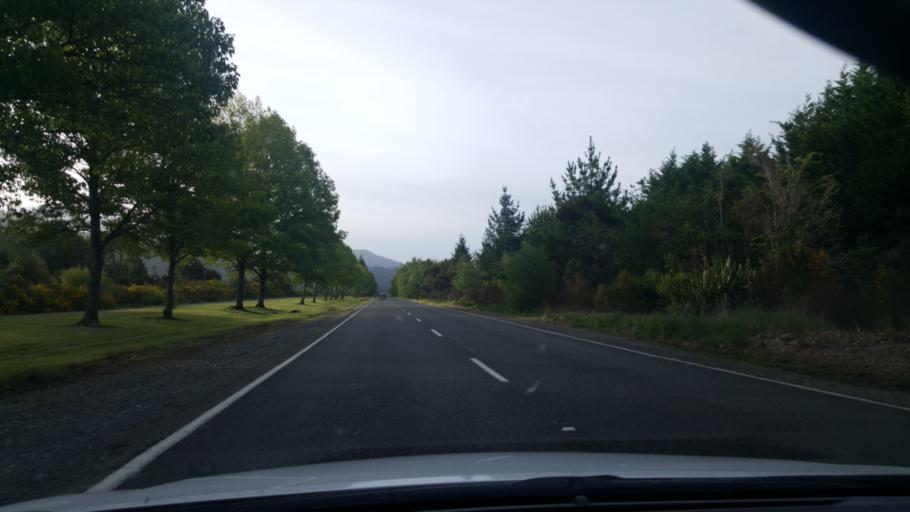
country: NZ
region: Waikato
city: Turangi
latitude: -38.9941
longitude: 175.7995
